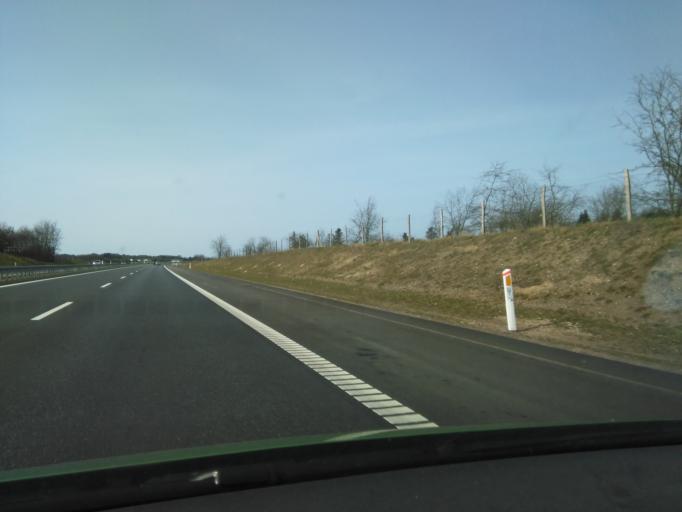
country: DK
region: Central Jutland
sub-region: Silkeborg Kommune
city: Svejbaek
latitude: 56.1474
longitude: 9.6751
